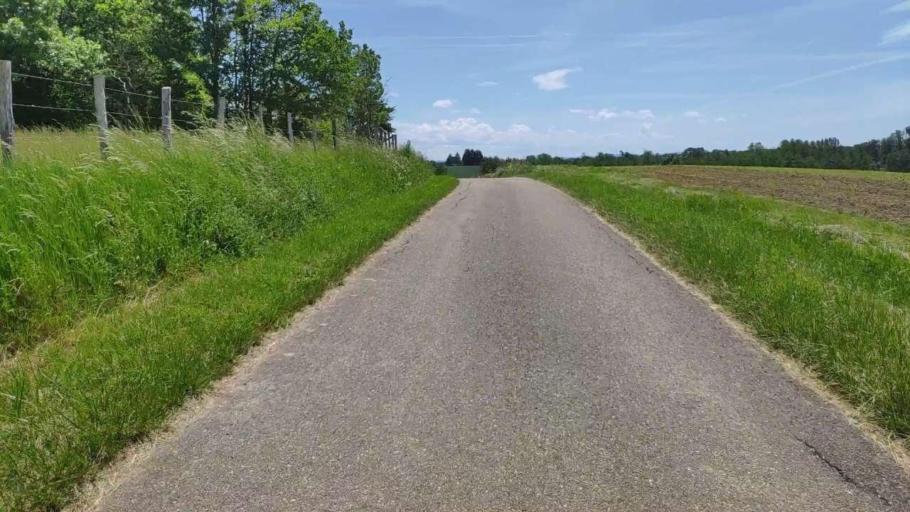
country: FR
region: Franche-Comte
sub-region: Departement du Jura
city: Bletterans
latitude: 46.7992
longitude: 5.3866
